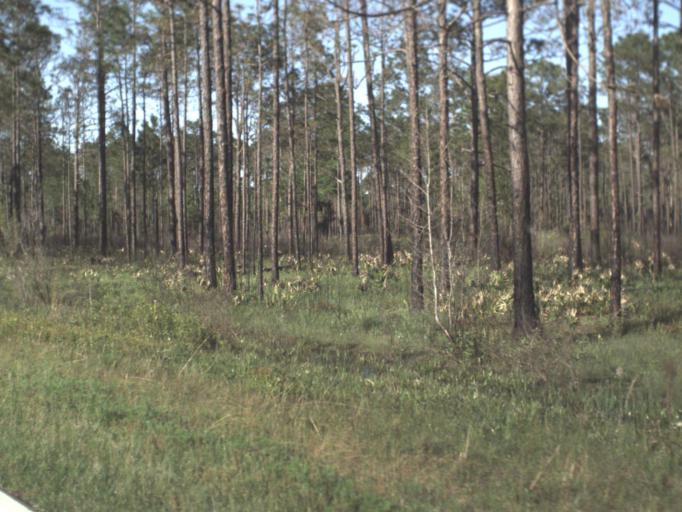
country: US
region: Florida
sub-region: Gulf County
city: Wewahitchka
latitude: 30.0373
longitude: -84.9835
